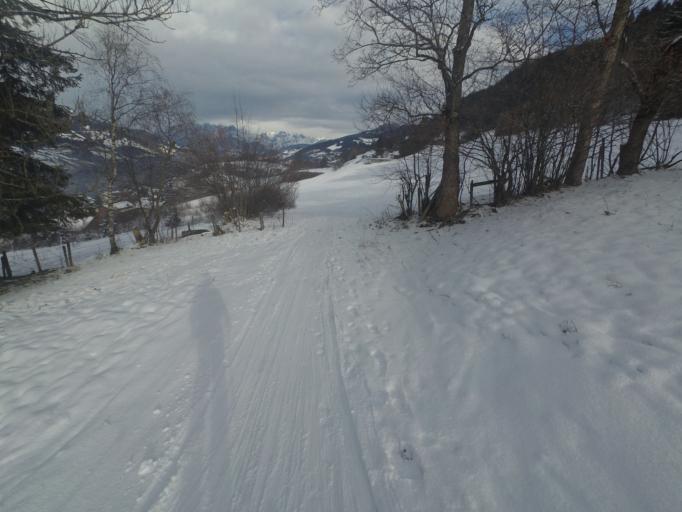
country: AT
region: Salzburg
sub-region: Politischer Bezirk Sankt Johann im Pongau
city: Sankt Johann im Pongau
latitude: 47.3233
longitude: 13.2026
